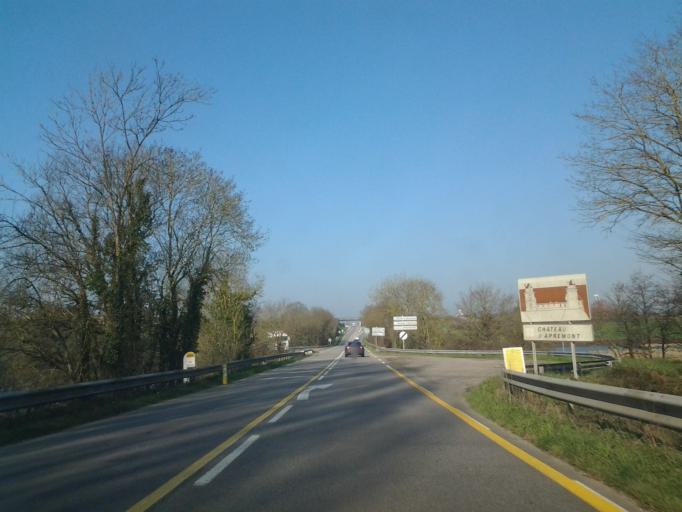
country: FR
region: Pays de la Loire
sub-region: Departement de la Vendee
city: Mache
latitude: 46.7694
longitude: -1.6649
